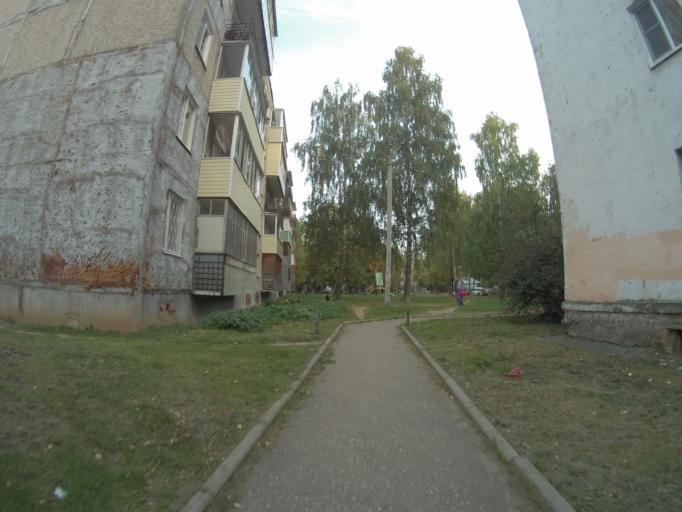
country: RU
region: Vladimir
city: Vladimir
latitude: 56.1412
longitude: 40.3875
